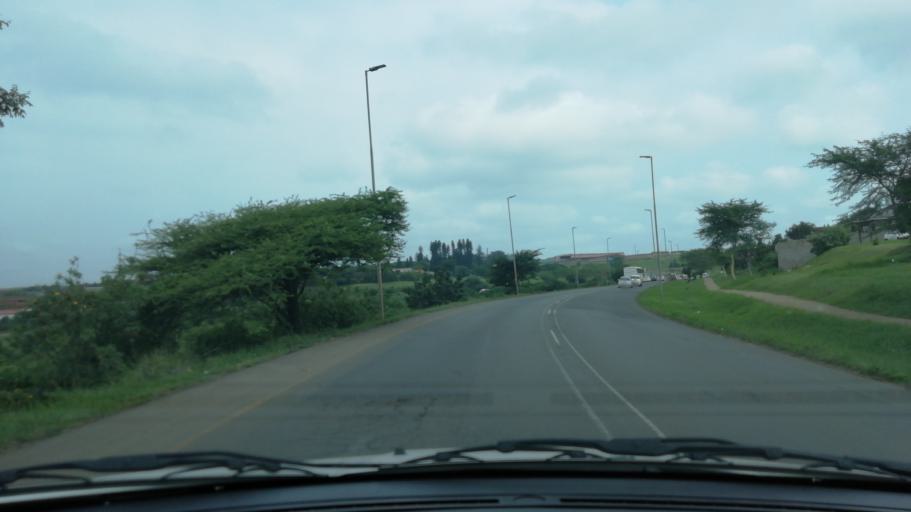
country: ZA
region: KwaZulu-Natal
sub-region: uThungulu District Municipality
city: Empangeni
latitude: -28.7384
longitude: 31.8812
